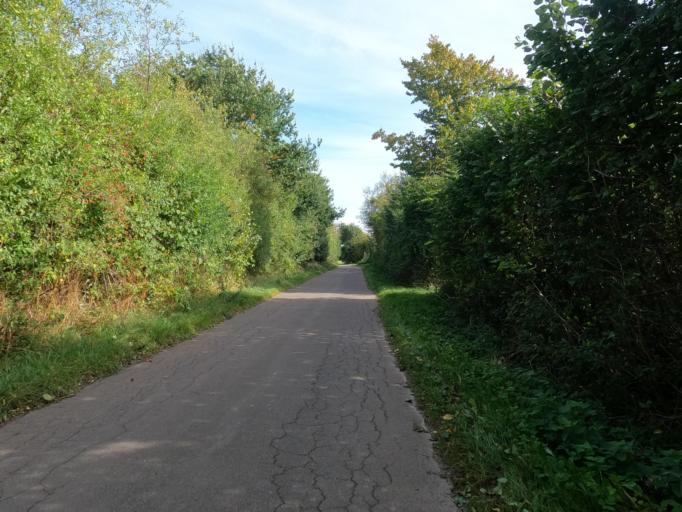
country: DE
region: Schleswig-Holstein
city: Riepsdorf
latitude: 54.2297
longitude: 10.9904
